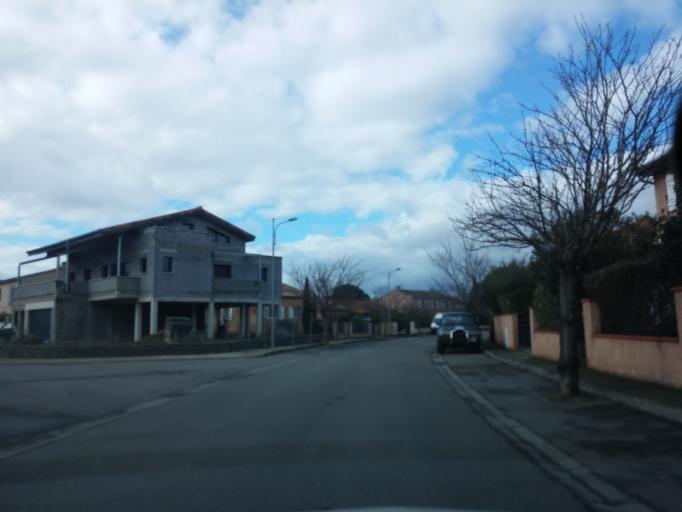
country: FR
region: Midi-Pyrenees
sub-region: Departement de la Haute-Garonne
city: Blagnac
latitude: 43.6412
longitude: 1.3983
